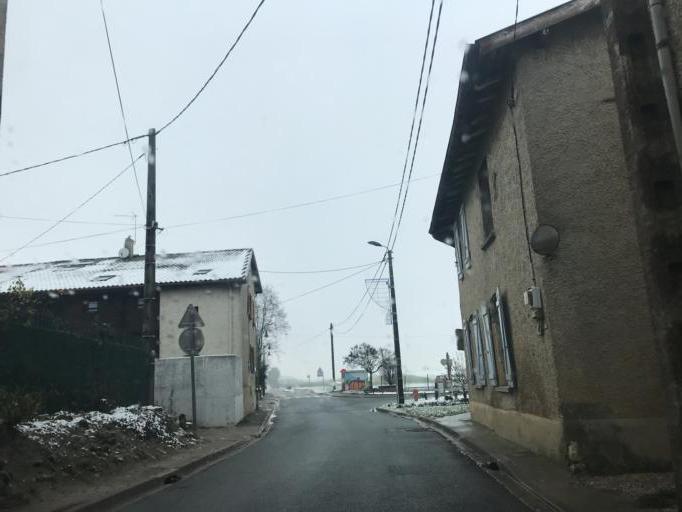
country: FR
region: Rhone-Alpes
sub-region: Departement de l'Ain
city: Miribel
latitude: 45.8323
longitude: 4.9470
